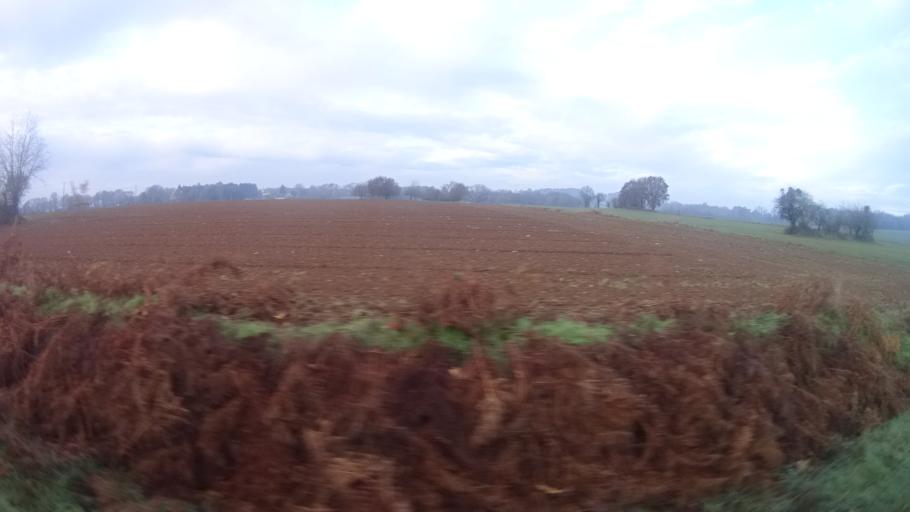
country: FR
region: Pays de la Loire
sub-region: Departement de la Loire-Atlantique
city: Avessac
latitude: 47.6498
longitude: -2.0240
